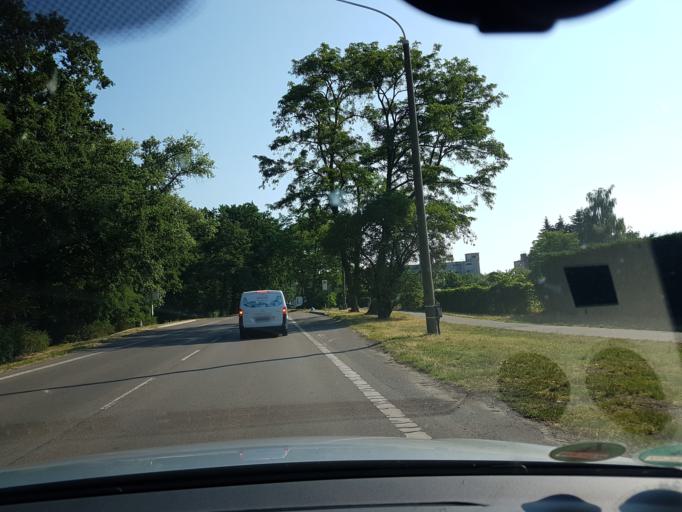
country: DE
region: Brandenburg
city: Brandenburg an der Havel
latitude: 52.3913
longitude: 12.5353
